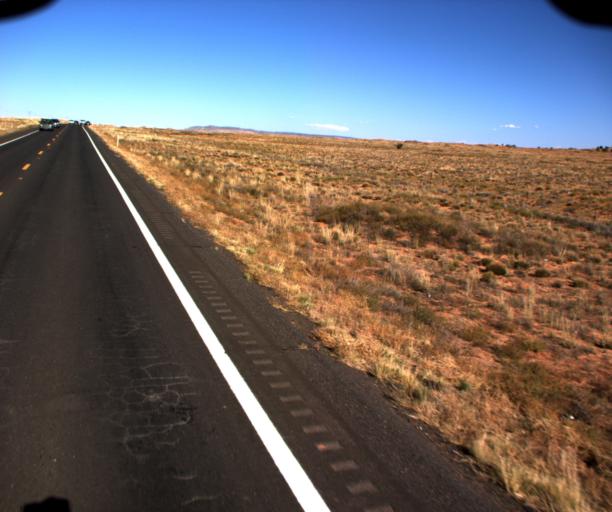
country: US
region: Arizona
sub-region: Coconino County
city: Tuba City
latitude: 36.2896
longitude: -110.9929
